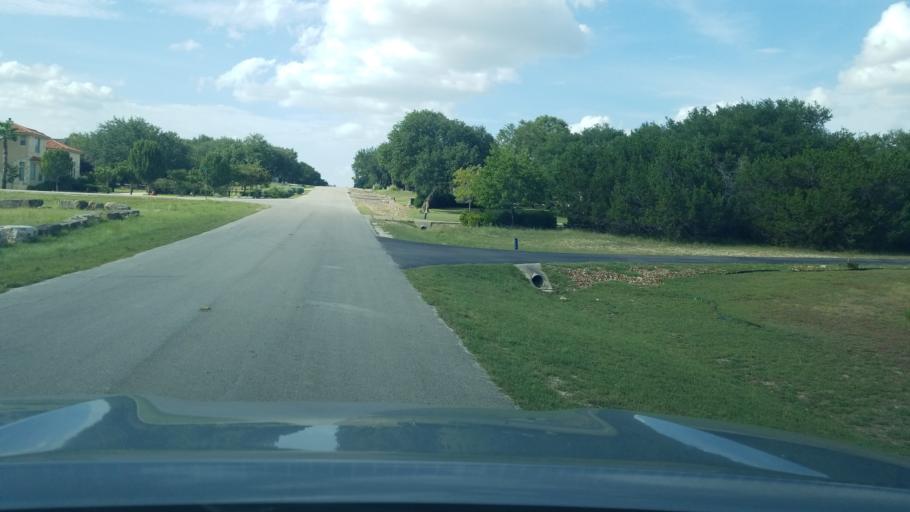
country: US
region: Texas
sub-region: Comal County
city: Bulverde
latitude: 29.8064
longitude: -98.3977
